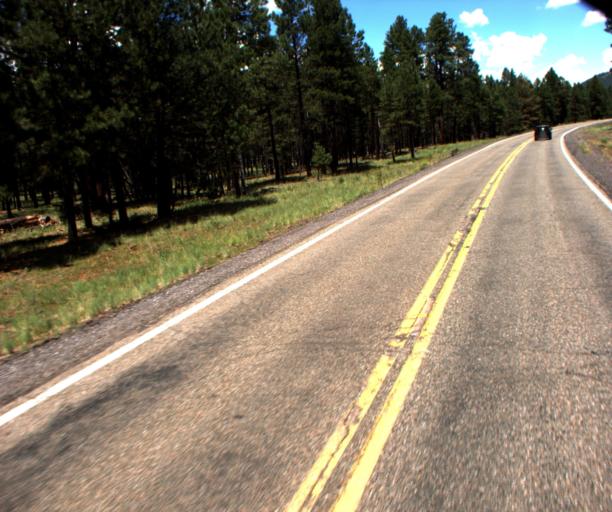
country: US
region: Arizona
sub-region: Coconino County
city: Flagstaff
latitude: 35.3182
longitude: -111.7750
